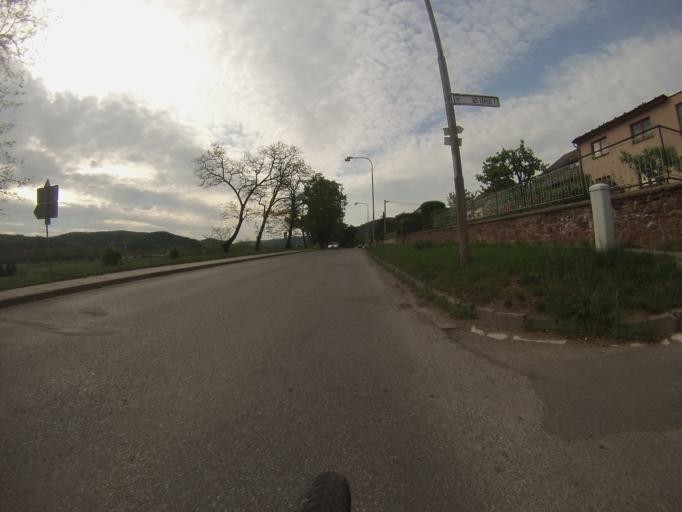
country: CZ
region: South Moravian
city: Tisnov
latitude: 49.3389
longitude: 16.4347
